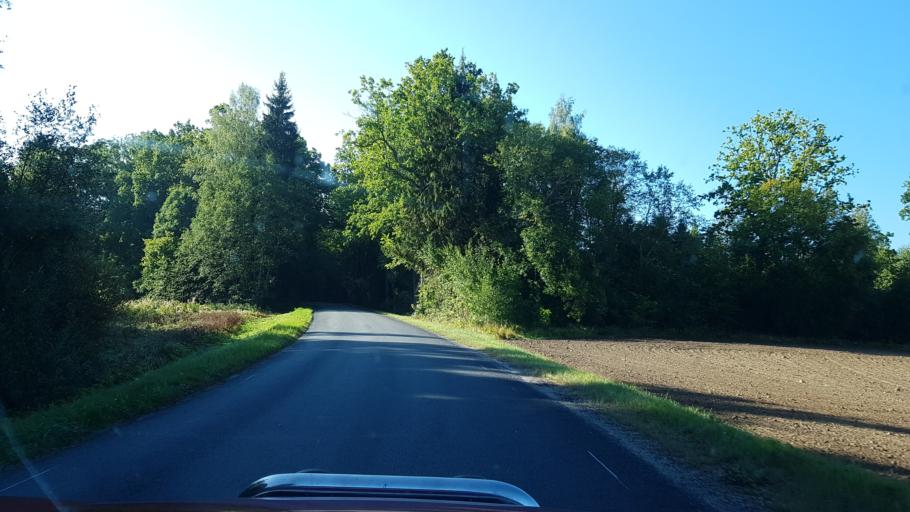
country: EE
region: Jogevamaa
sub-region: Jogeva linn
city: Jogeva
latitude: 58.7262
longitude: 26.5163
